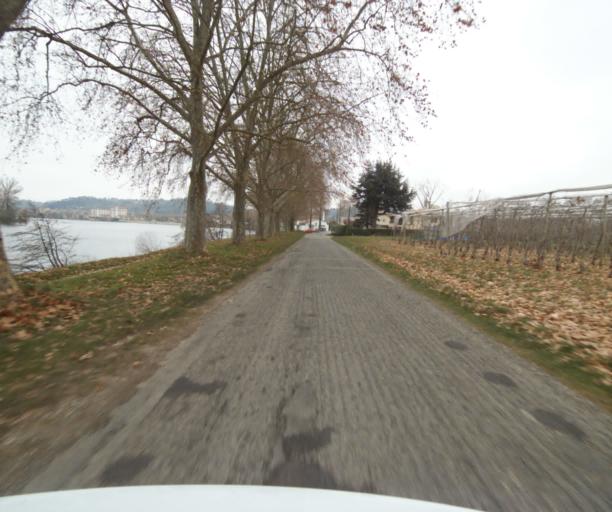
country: FR
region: Midi-Pyrenees
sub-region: Departement du Tarn-et-Garonne
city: Moissac
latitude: 44.0963
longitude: 1.0938
